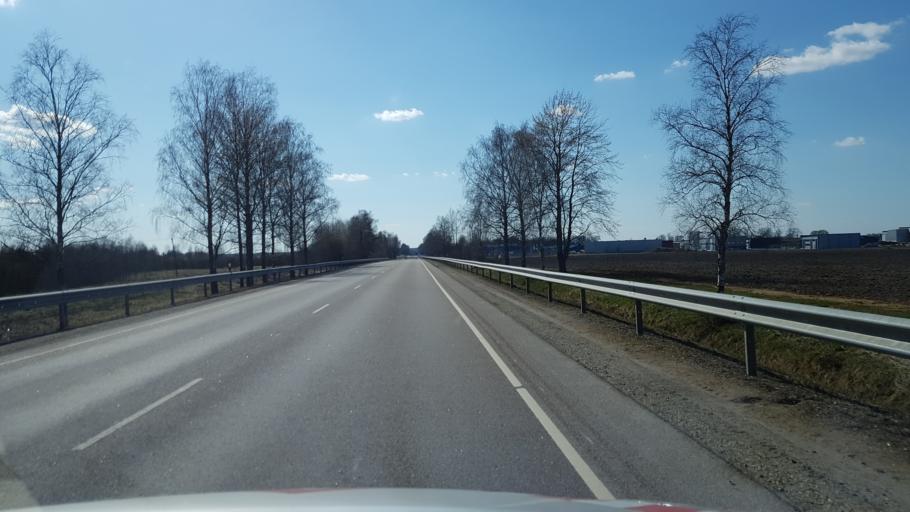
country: EE
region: Tartu
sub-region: Tartu linn
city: Tartu
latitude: 58.4137
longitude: 26.7351
